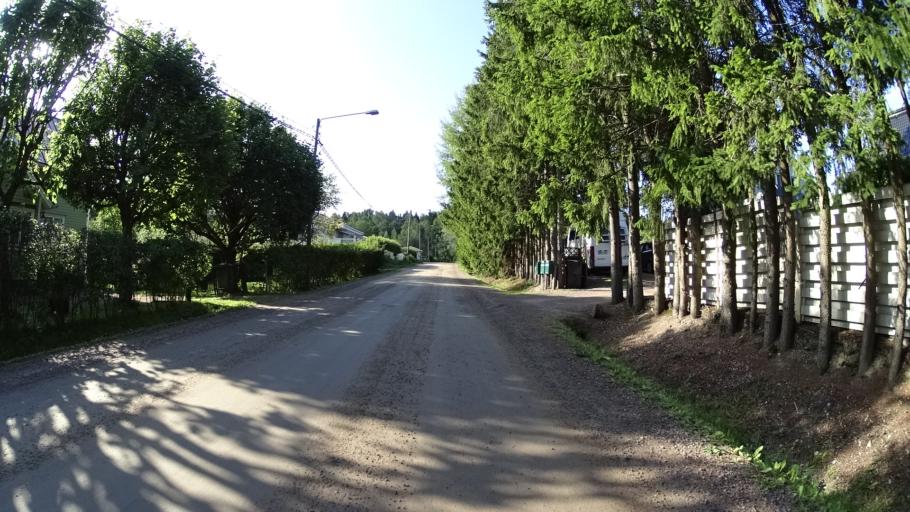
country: FI
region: Uusimaa
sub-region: Helsinki
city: Kilo
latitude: 60.2365
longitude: 24.7682
